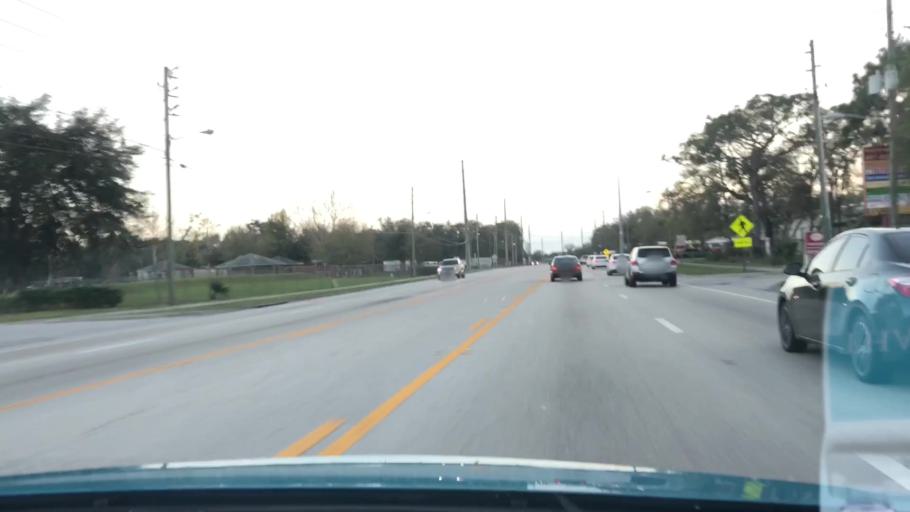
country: US
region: Florida
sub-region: Osceola County
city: Buenaventura Lakes
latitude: 28.3362
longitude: -81.3902
